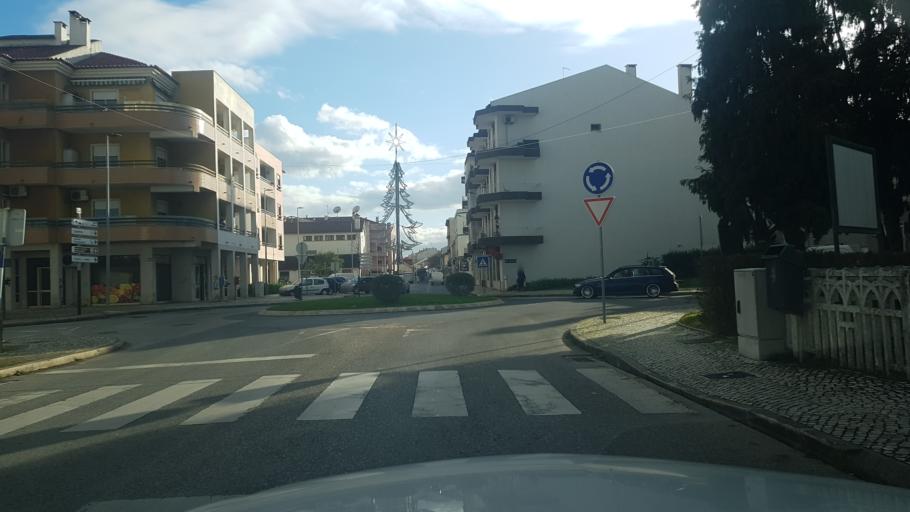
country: PT
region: Santarem
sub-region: Entroncamento
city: Entroncamento
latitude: 39.4688
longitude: -8.4732
